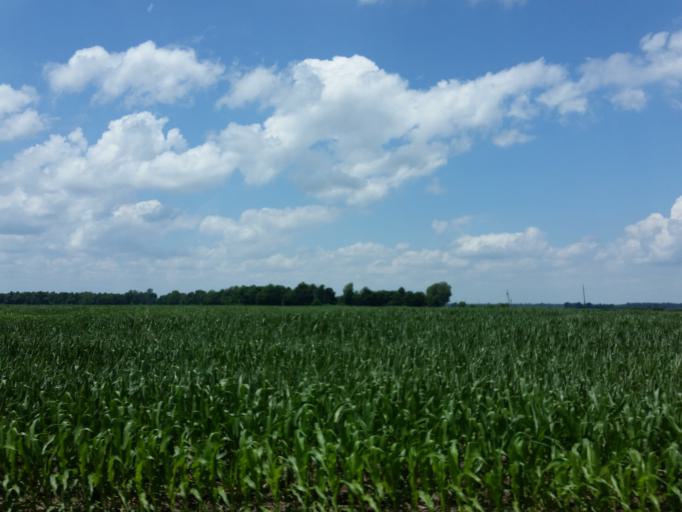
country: US
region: Kentucky
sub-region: Fulton County
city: Hickman
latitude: 36.5323
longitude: -89.3387
